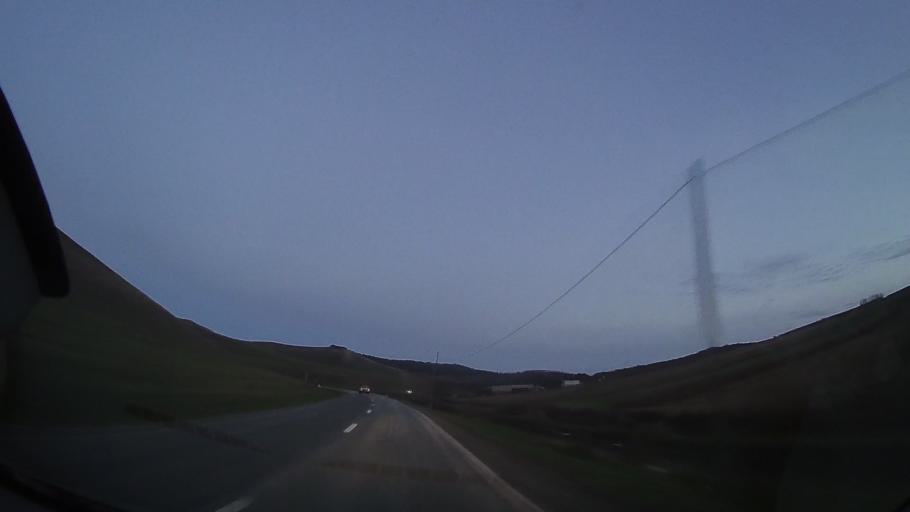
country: RO
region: Cluj
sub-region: Comuna Camarasu
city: Camarasu
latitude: 46.7977
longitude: 24.1680
